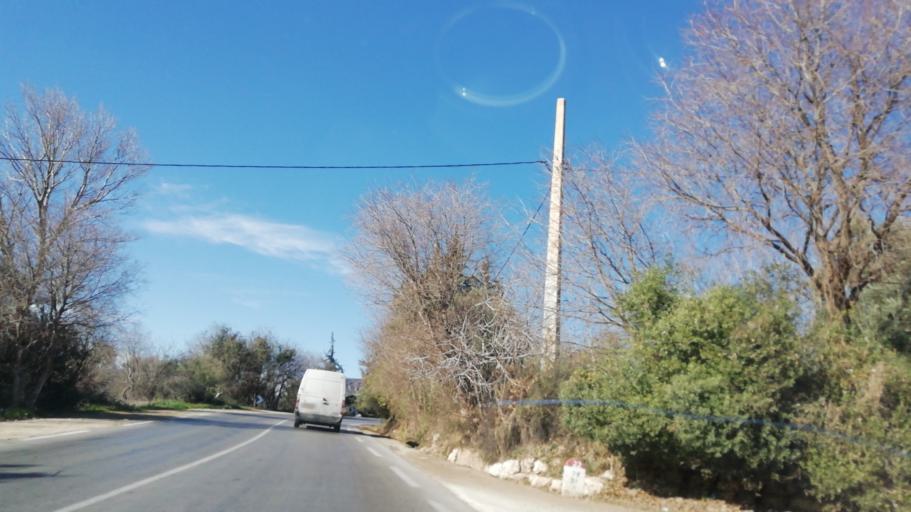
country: DZ
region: Tlemcen
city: Sebdou
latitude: 34.6821
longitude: -1.3134
